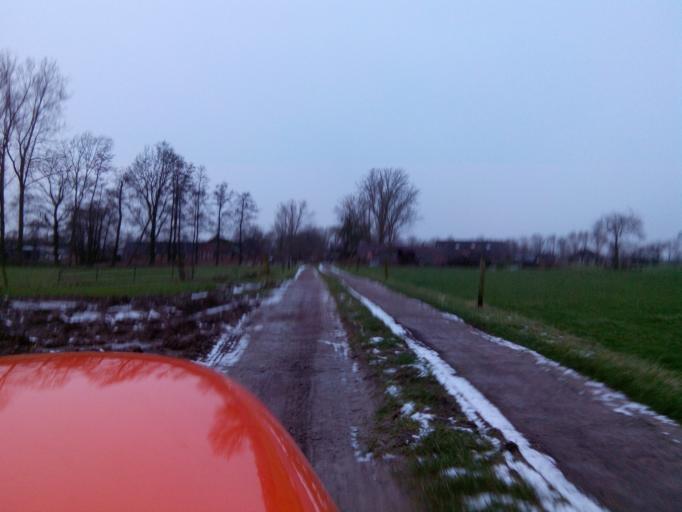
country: NL
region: Gelderland
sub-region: Gemeente Barneveld
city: Zwartebroek
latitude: 52.1546
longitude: 5.4841
